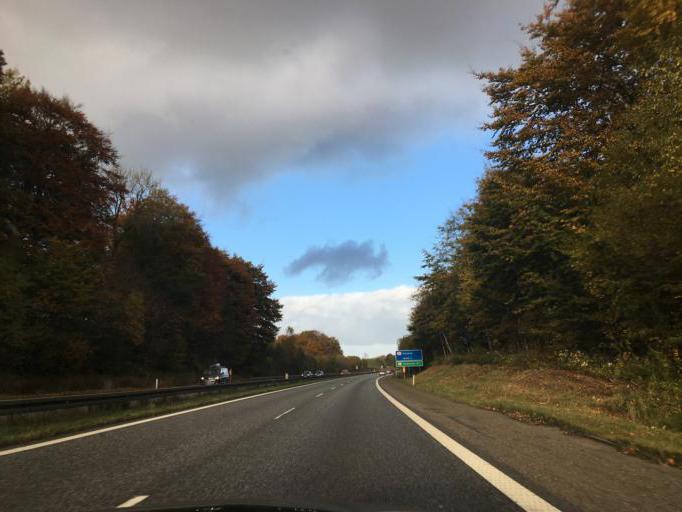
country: DK
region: South Denmark
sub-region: Haderslev Kommune
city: Vojens
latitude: 55.2338
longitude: 9.3851
